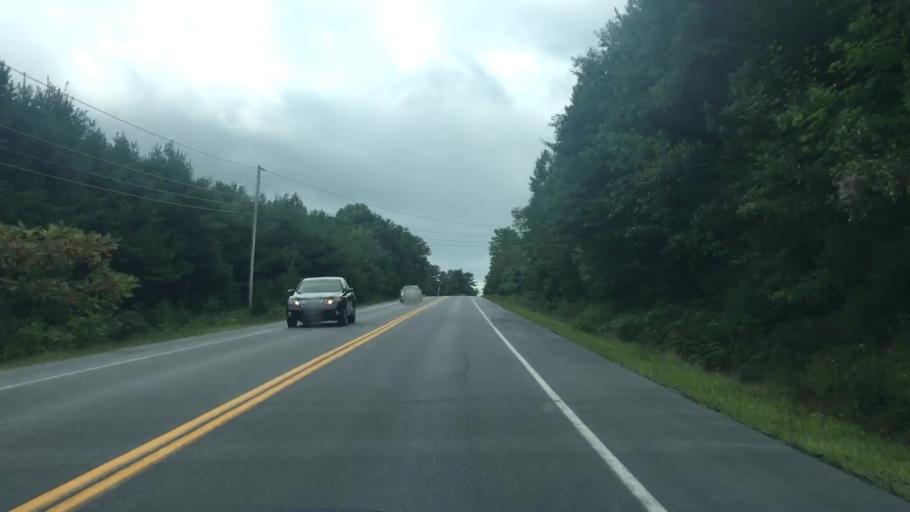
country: US
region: Maine
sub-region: York County
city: Cornish
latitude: 43.7506
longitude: -70.8125
